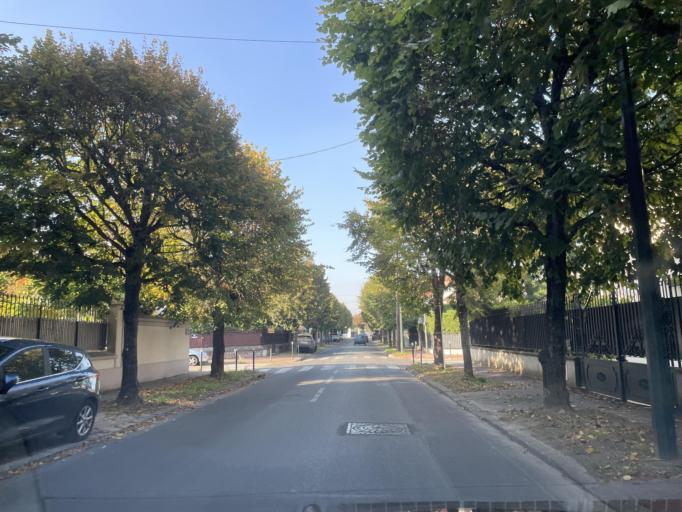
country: FR
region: Ile-de-France
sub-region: Departement du Val-de-Marne
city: Chennevieres-sur-Marne
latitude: 48.8042
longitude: 2.5179
